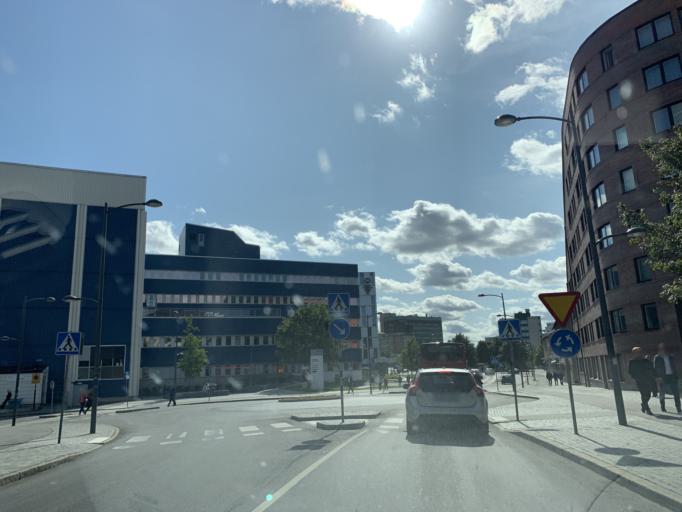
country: SE
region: Stockholm
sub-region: Sundbybergs Kommun
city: Sundbyberg
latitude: 59.3584
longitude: 17.9748
